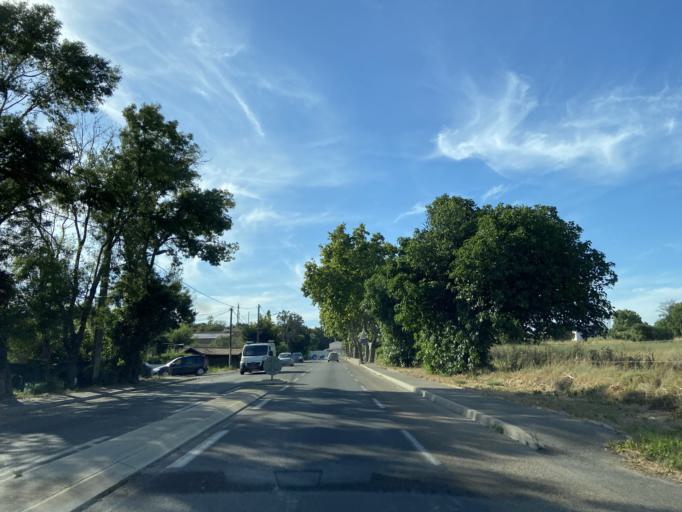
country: FR
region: Provence-Alpes-Cote d'Azur
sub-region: Departement des Bouches-du-Rhone
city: Miramas
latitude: 43.5752
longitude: 5.0163
